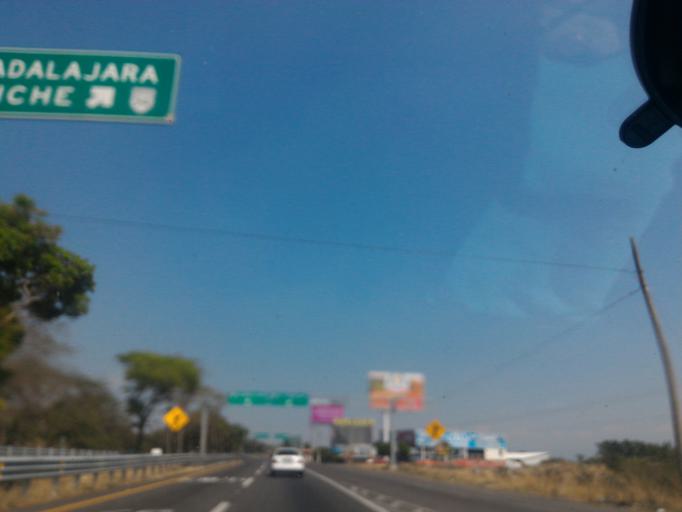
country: MX
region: Colima
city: Colima
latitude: 19.2698
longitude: -103.6733
